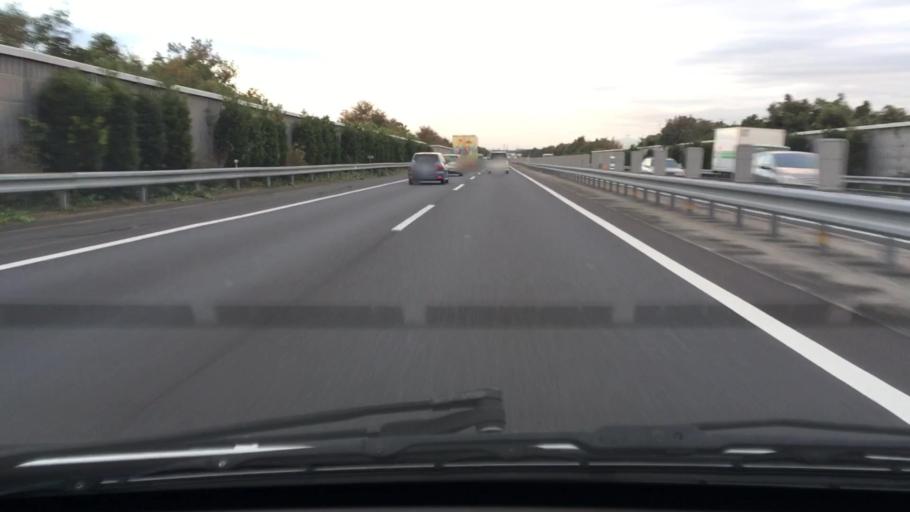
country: JP
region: Chiba
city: Ichihara
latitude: 35.5291
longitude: 140.1300
